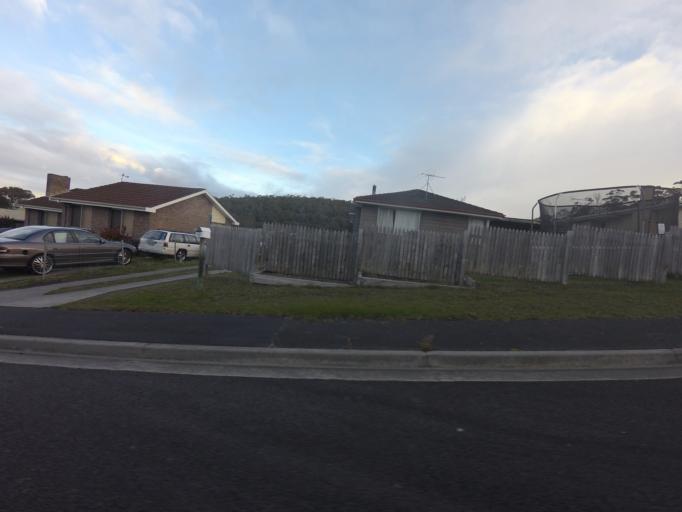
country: AU
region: Tasmania
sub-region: Clarence
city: Rokeby
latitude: -42.9029
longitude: 147.4265
